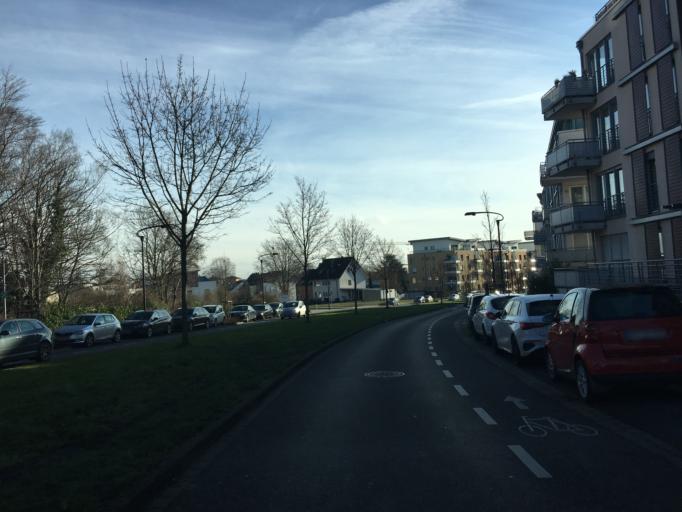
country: DE
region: North Rhine-Westphalia
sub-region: Regierungsbezirk Koln
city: Hurth
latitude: 50.8781
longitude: 6.8809
